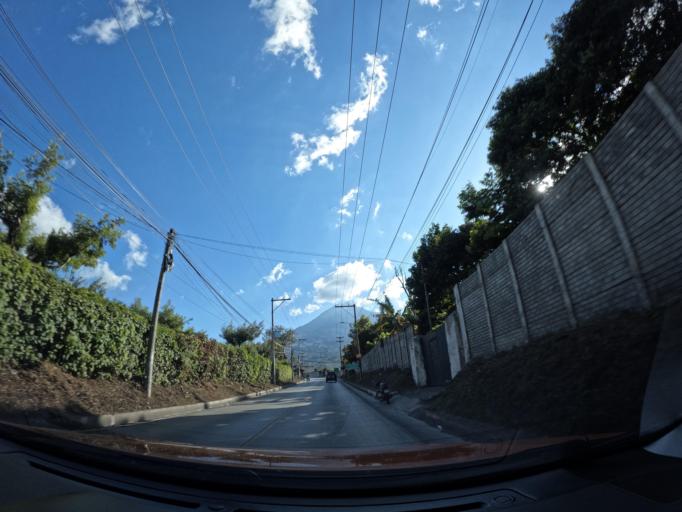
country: GT
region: Sacatepequez
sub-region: Municipio de Santa Maria de Jesus
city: Santa Maria de Jesus
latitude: 14.5360
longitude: -90.7298
